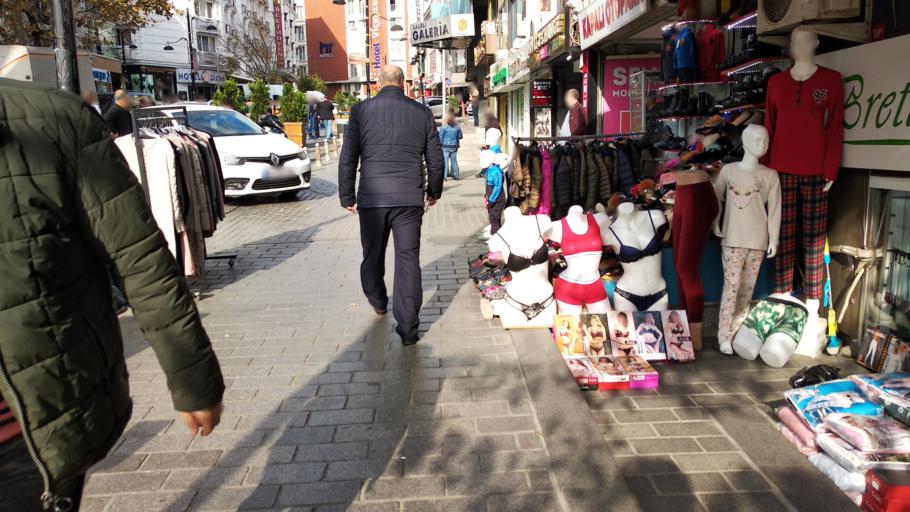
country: TR
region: Istanbul
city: Istanbul
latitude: 41.0110
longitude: 28.9575
